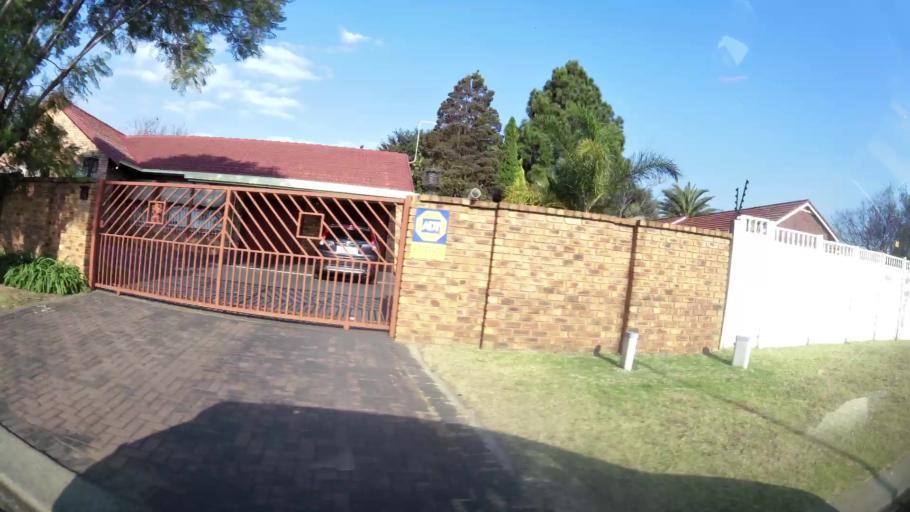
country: ZA
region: Gauteng
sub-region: Ekurhuleni Metropolitan Municipality
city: Benoni
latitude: -26.1282
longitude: 28.3645
